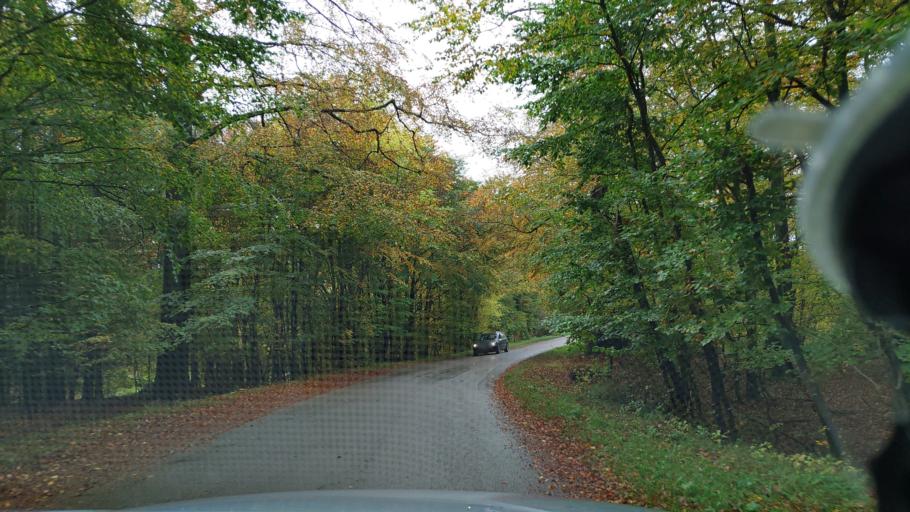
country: DK
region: Zealand
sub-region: Faxe Kommune
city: Ronnede
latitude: 55.2520
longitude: 11.9588
